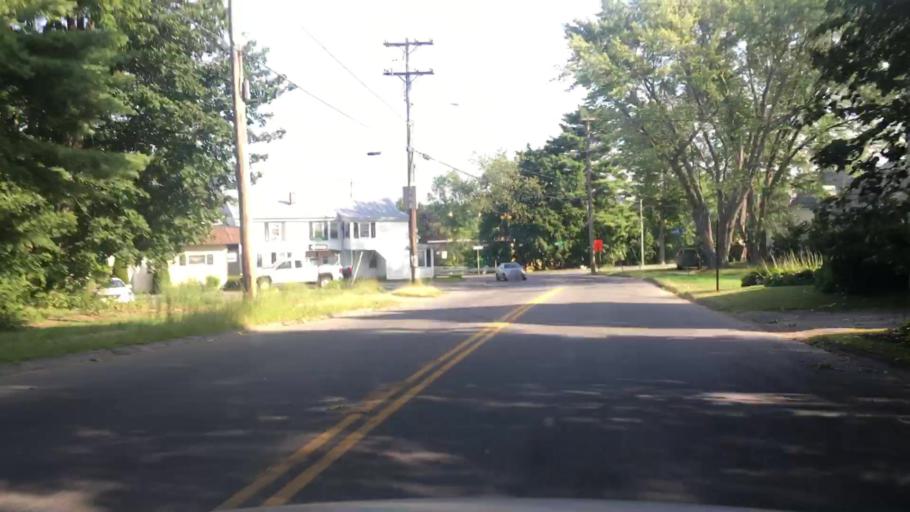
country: US
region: Maine
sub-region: Kennebec County
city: Waterville
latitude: 44.5490
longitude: -69.6435
